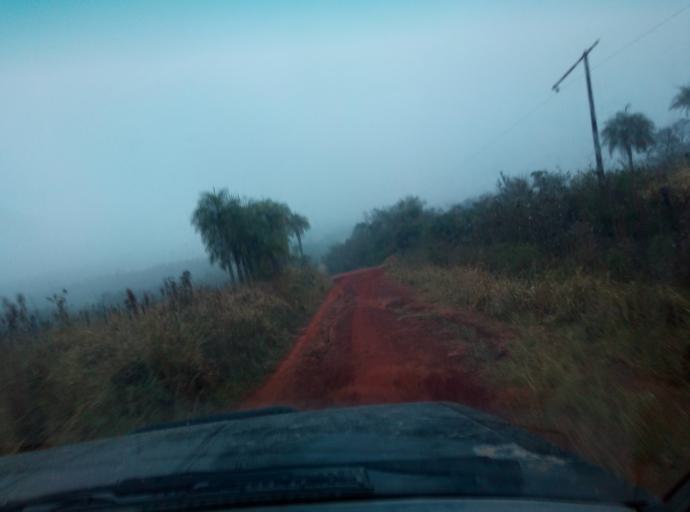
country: PY
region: Caaguazu
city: Doctor Cecilio Baez
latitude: -25.1584
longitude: -56.2544
